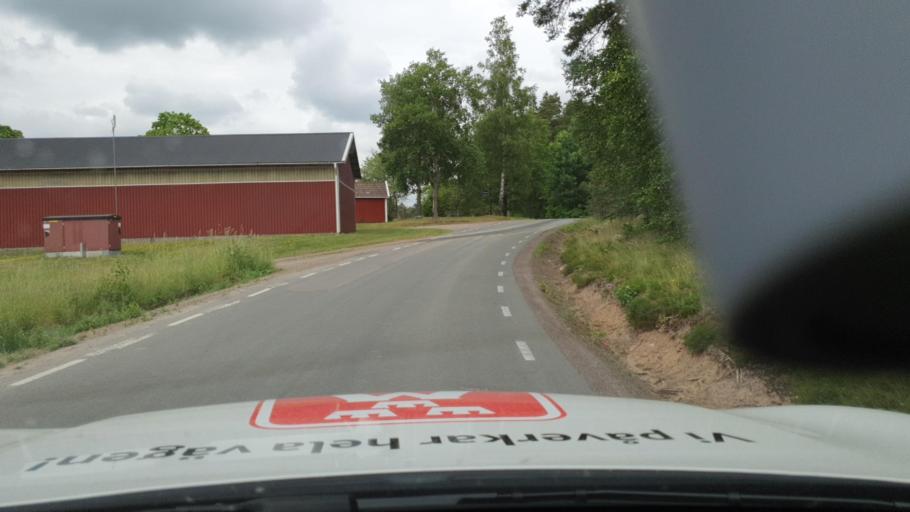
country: SE
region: Vaestra Goetaland
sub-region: Tidaholms Kommun
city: Olofstorp
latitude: 58.2910
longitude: 14.1046
